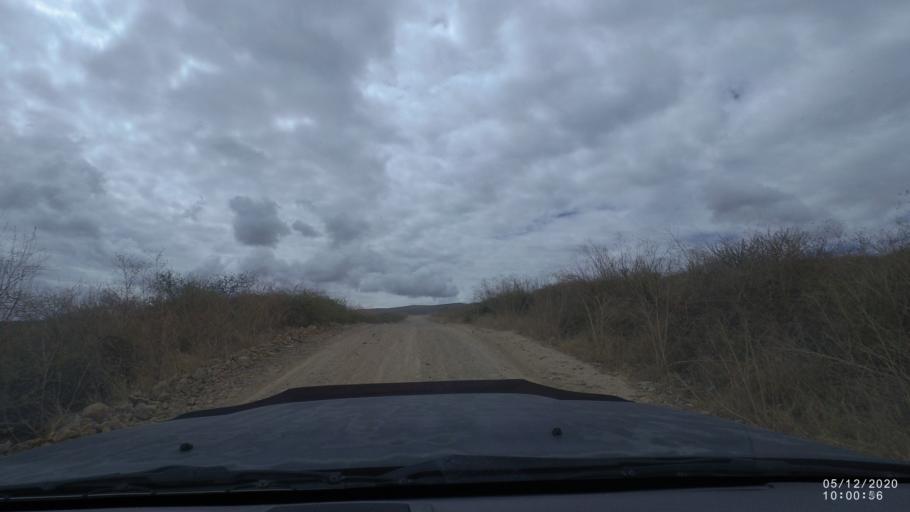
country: BO
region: Cochabamba
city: Sipe Sipe
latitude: -17.4393
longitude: -66.2850
